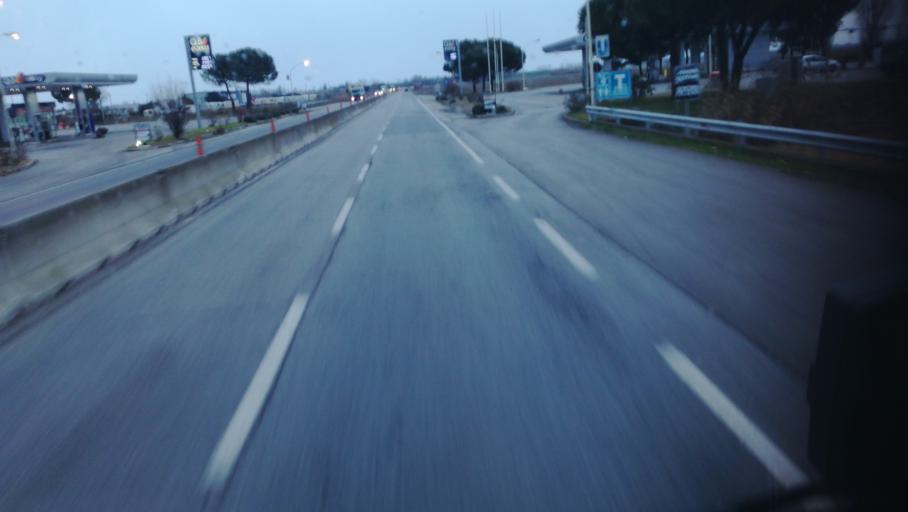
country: IT
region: Emilia-Romagna
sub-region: Provincia di Ravenna
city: Classe
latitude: 44.3759
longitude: 12.2224
